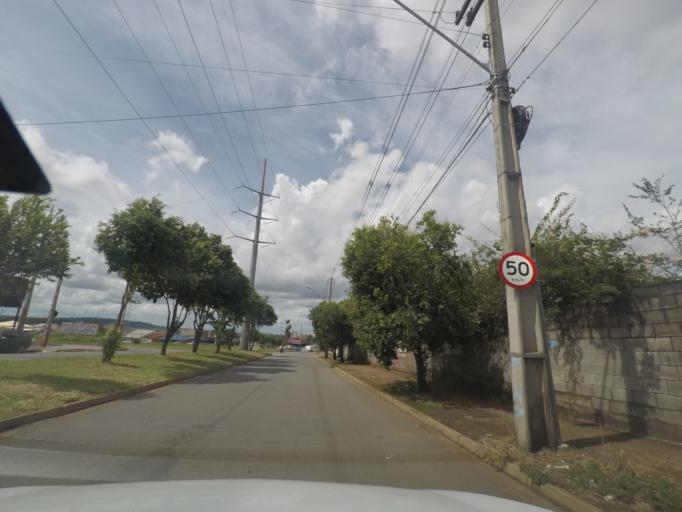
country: BR
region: Goias
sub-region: Goiania
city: Goiania
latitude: -16.7281
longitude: -49.3396
